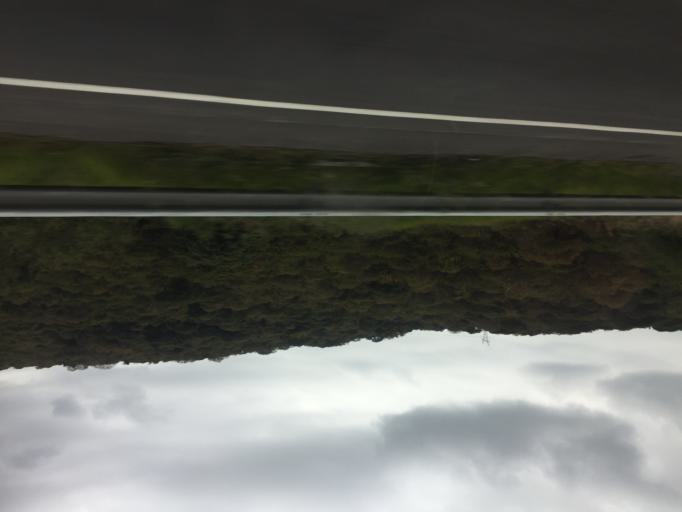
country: MX
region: Jalisco
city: Ocotlan
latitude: 20.4313
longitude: -102.7856
